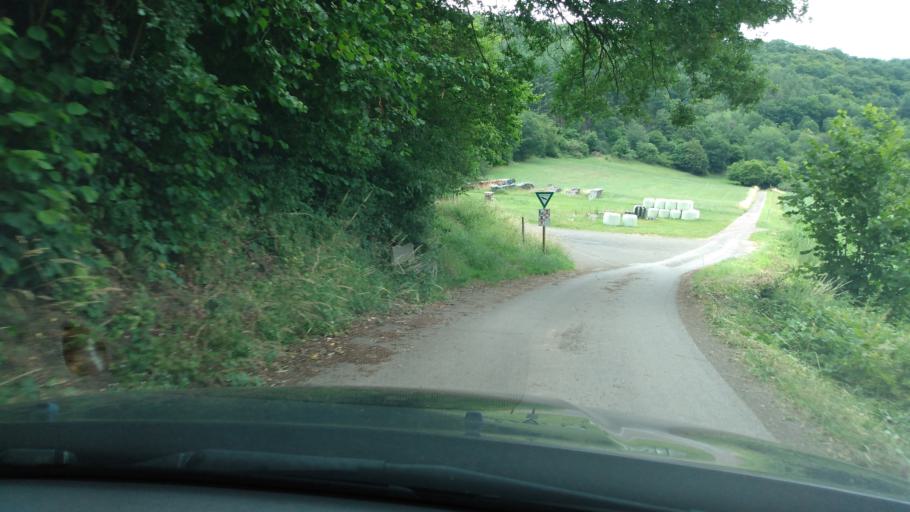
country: DE
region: Rheinland-Pfalz
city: Meerfeld
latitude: 50.0967
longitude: 6.7509
